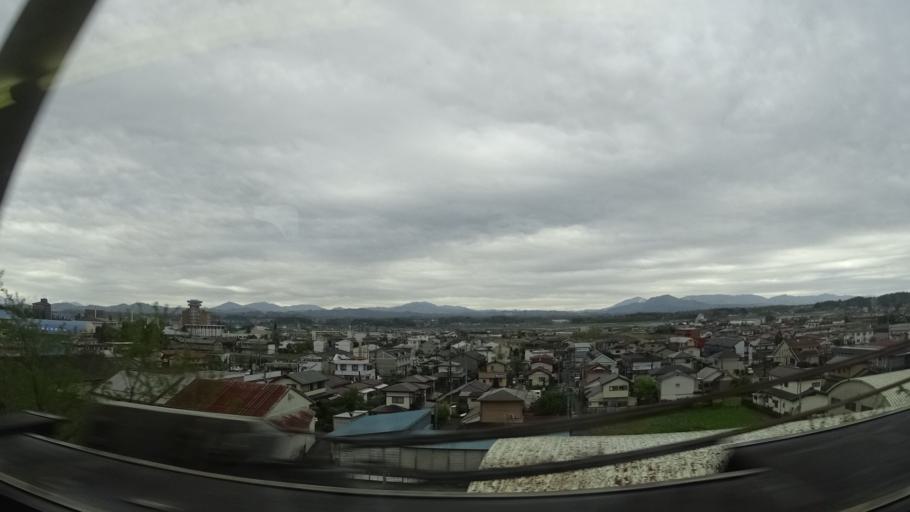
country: JP
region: Fukushima
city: Koriyama
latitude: 37.3571
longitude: 140.3745
